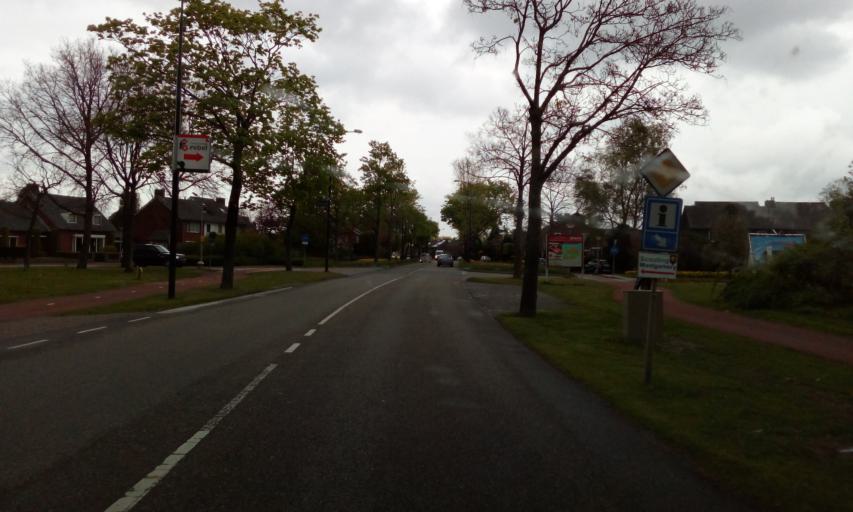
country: NL
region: North Holland
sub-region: Gemeente Huizen
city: Huizen
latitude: 52.2889
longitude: 5.2394
